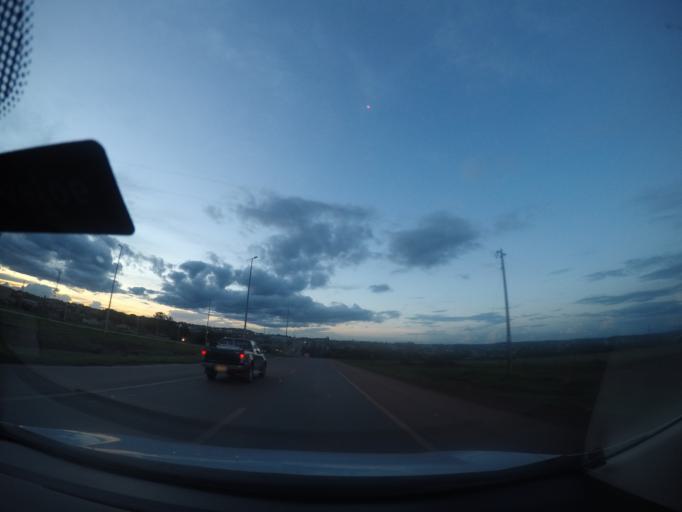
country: BR
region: Goias
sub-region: Goianira
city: Goianira
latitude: -16.5140
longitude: -49.4181
